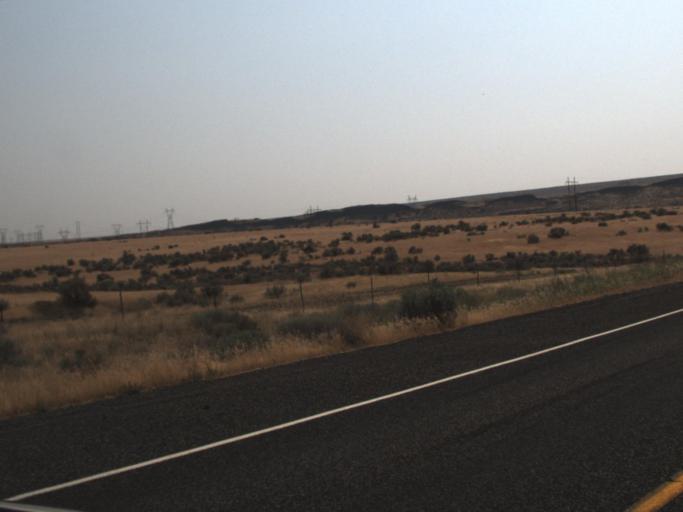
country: US
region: Washington
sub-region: Grant County
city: Desert Aire
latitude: 46.6209
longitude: -119.7266
